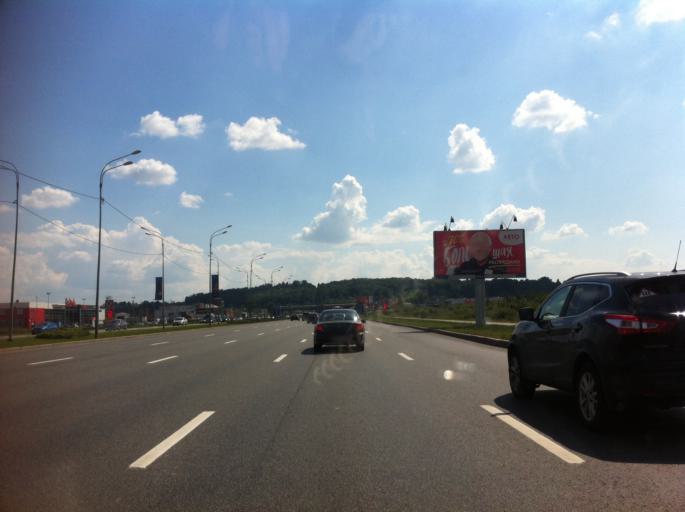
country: RU
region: St.-Petersburg
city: Aleksandrovskaya
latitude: 59.7853
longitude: 30.3248
